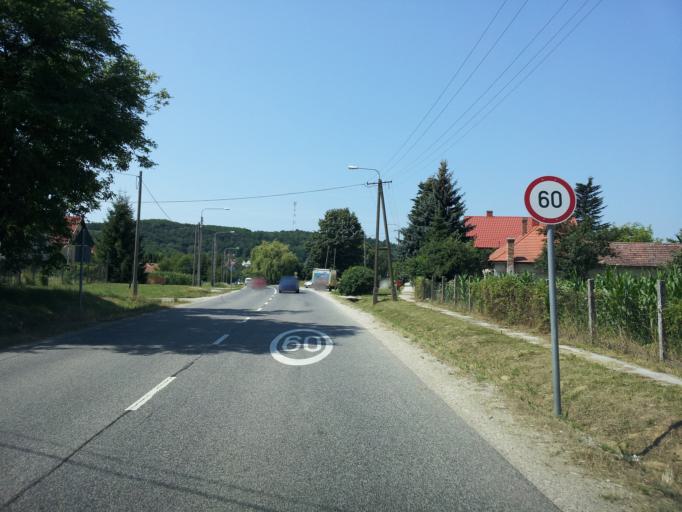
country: HU
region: Zala
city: Pacsa
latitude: 46.8213
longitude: 17.0059
